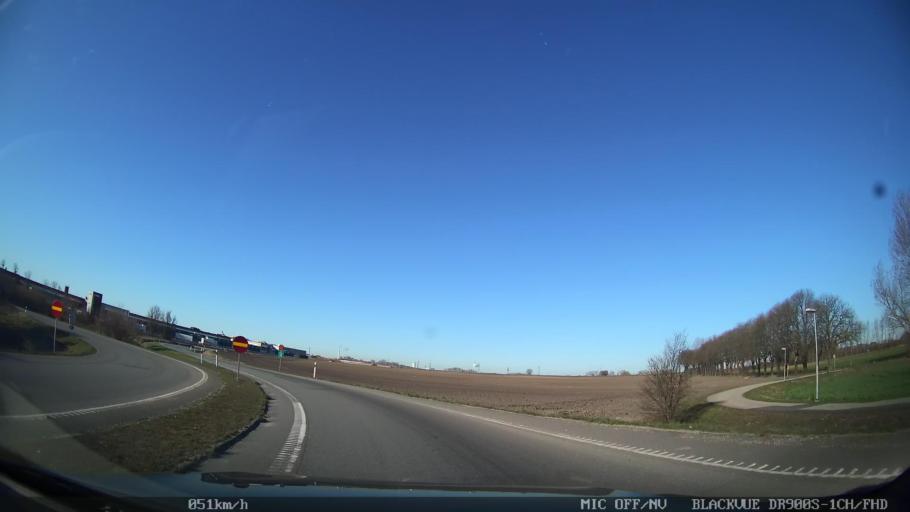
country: SE
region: Skane
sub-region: Burlovs Kommun
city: Arloev
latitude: 55.6488
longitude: 13.0775
